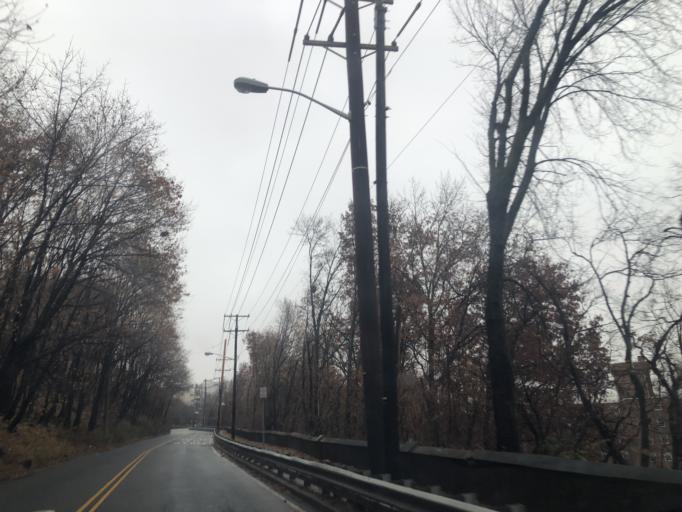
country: US
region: New Jersey
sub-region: Hudson County
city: Hoboken
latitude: 40.7439
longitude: -74.0425
